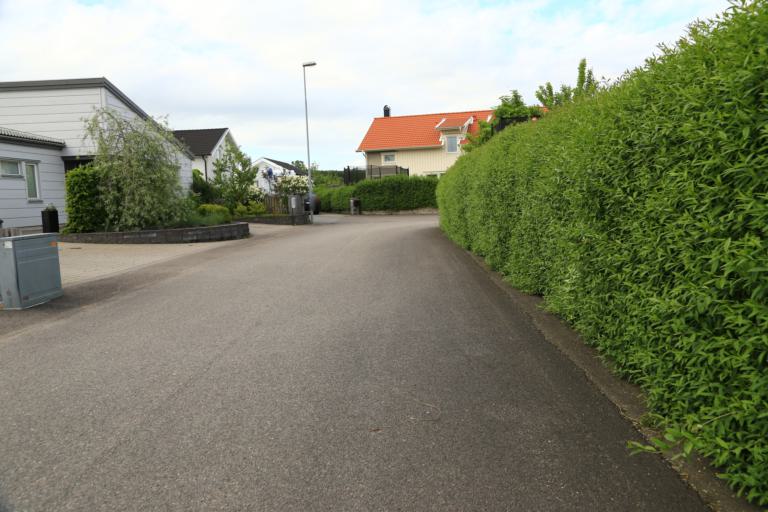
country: SE
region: Halland
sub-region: Varbergs Kommun
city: Traslovslage
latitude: 57.0871
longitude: 12.2802
